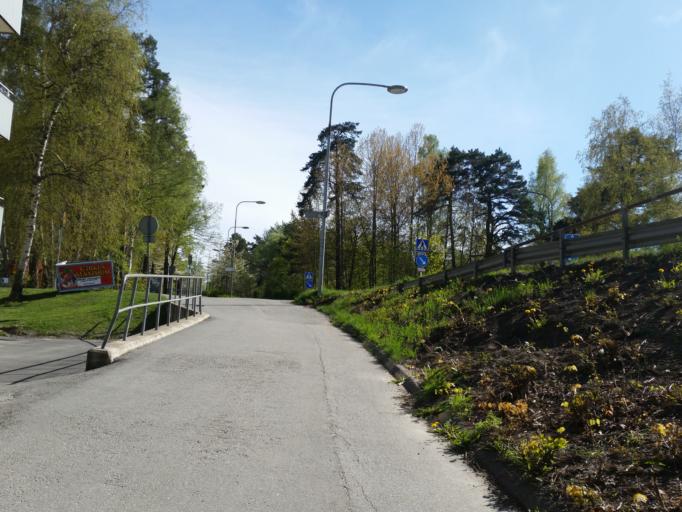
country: SE
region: Stockholm
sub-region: Stockholms Kommun
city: Arsta
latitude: 59.2888
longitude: 18.1009
